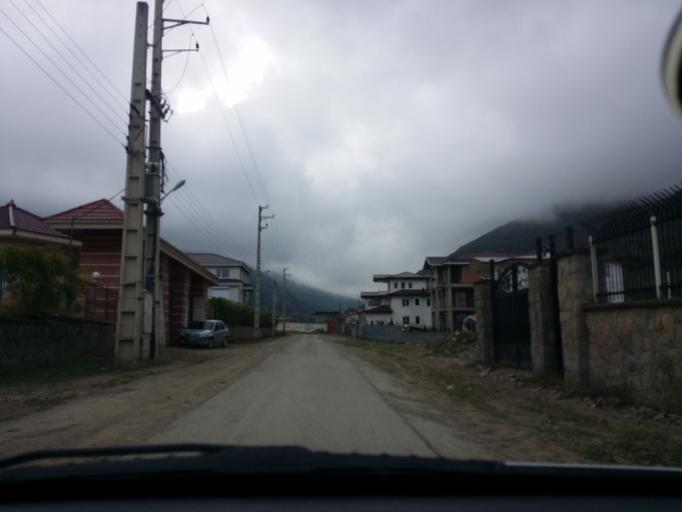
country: IR
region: Mazandaran
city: `Abbasabad
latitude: 36.4886
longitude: 51.1359
